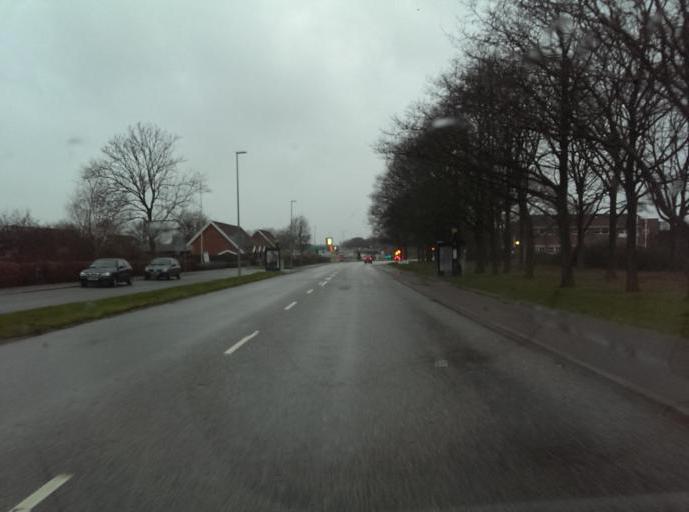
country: DK
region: South Denmark
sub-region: Esbjerg Kommune
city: Esbjerg
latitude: 55.4868
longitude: 8.4694
